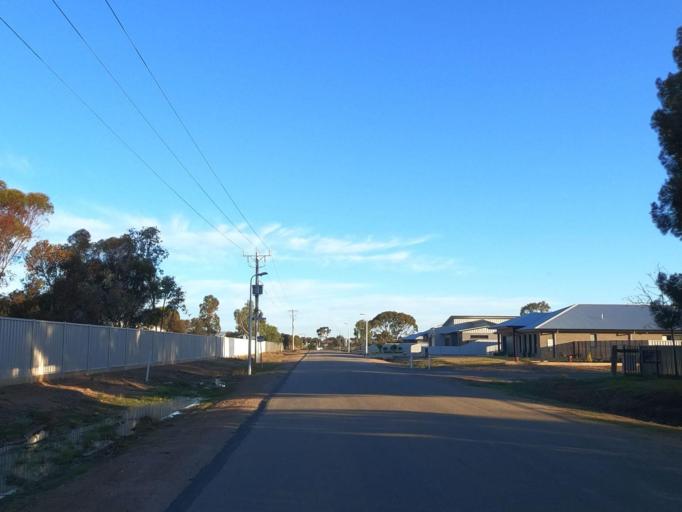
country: AU
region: Victoria
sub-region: Swan Hill
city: Swan Hill
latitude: -35.3312
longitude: 143.5344
